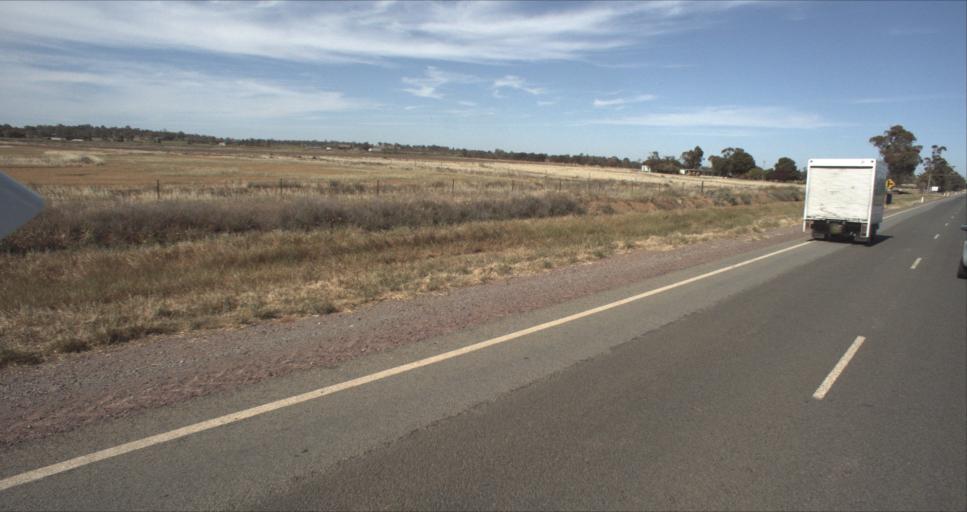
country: AU
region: New South Wales
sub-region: Leeton
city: Leeton
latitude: -34.5584
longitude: 146.4437
